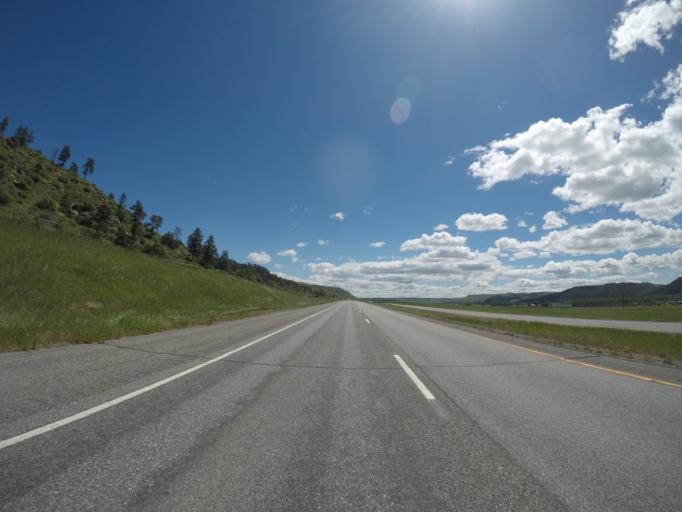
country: US
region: Montana
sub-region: Stillwater County
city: Columbus
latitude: 45.6020
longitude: -109.1433
